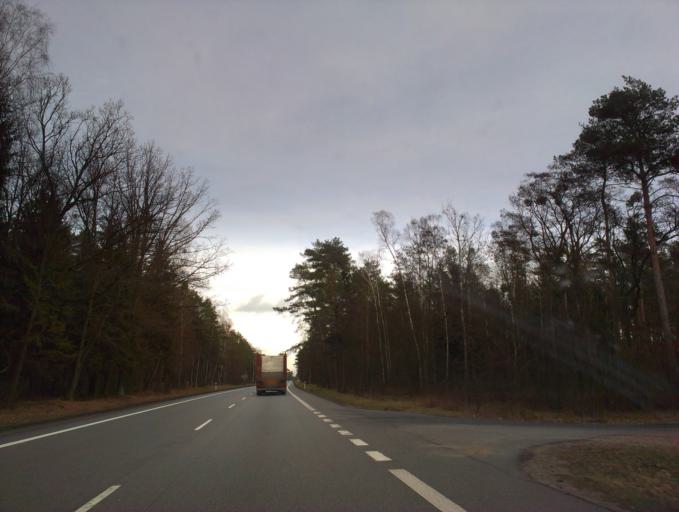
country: PL
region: Kujawsko-Pomorskie
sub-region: Powiat lipnowski
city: Skepe
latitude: 52.8838
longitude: 19.3891
